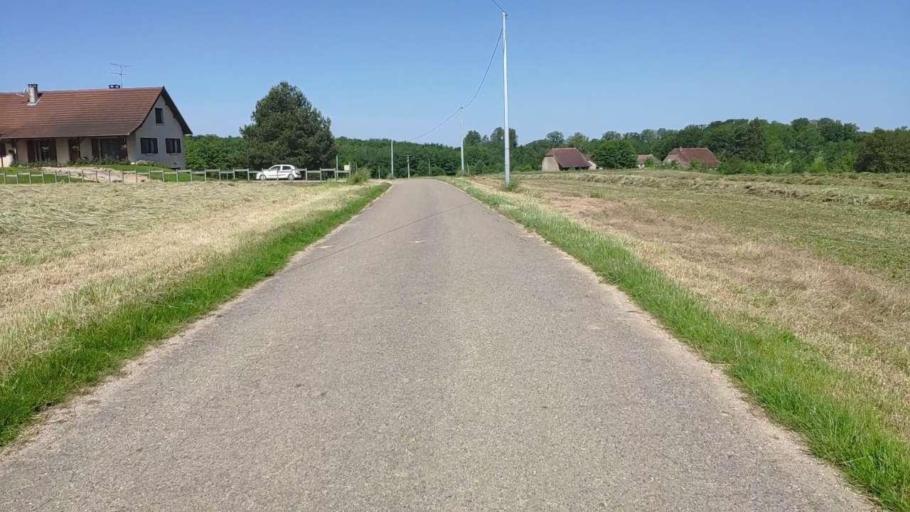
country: FR
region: Franche-Comte
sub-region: Departement du Jura
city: Bletterans
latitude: 46.7904
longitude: 5.4365
